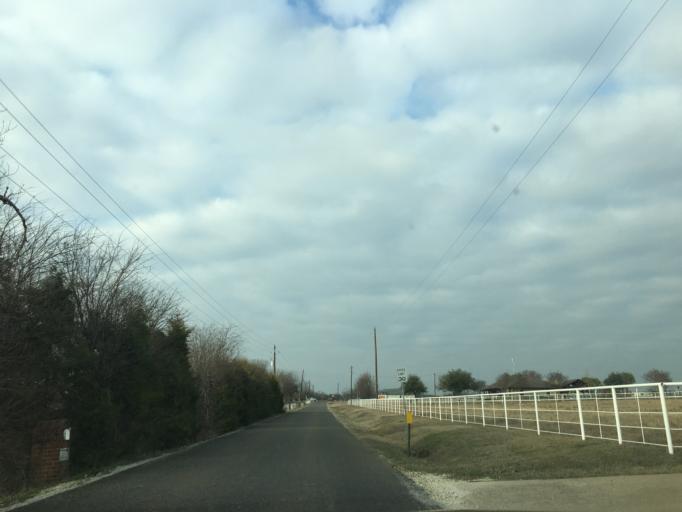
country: US
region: Texas
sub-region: Ellis County
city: Red Oak
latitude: 32.4819
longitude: -96.7897
